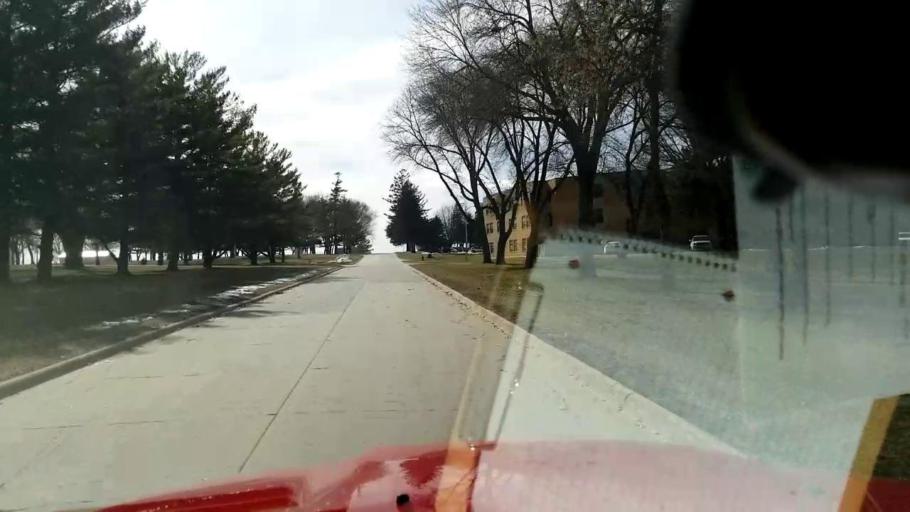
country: US
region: Iowa
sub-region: Buchanan County
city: Independence
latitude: 42.4542
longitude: -91.9235
